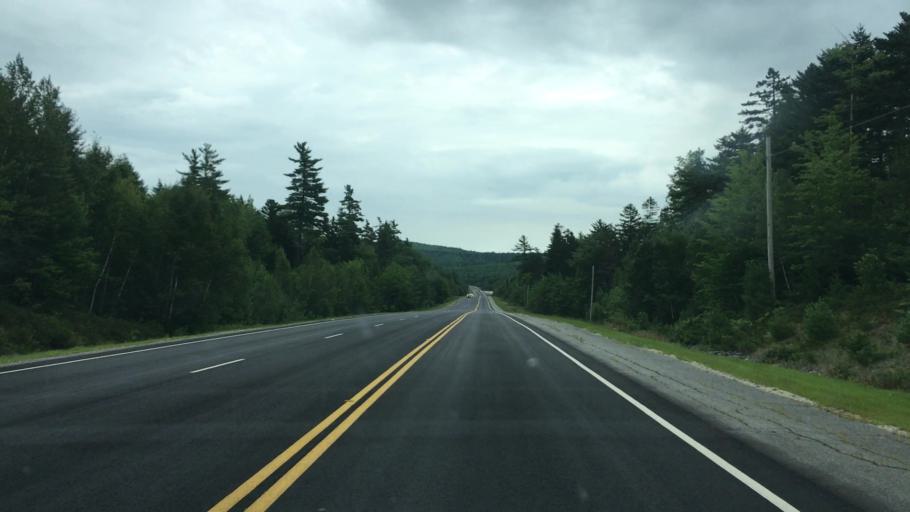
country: US
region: Maine
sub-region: Washington County
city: Cherryfield
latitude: 44.8771
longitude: -67.8825
